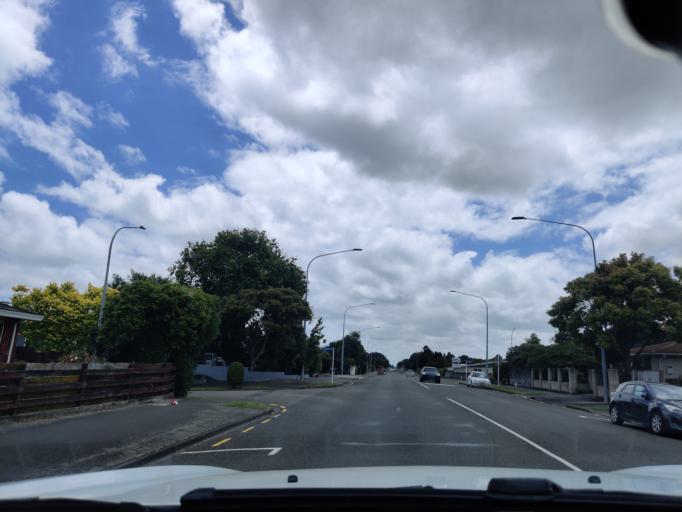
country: NZ
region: Manawatu-Wanganui
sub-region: Palmerston North City
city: Palmerston North
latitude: -40.3602
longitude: 175.6317
